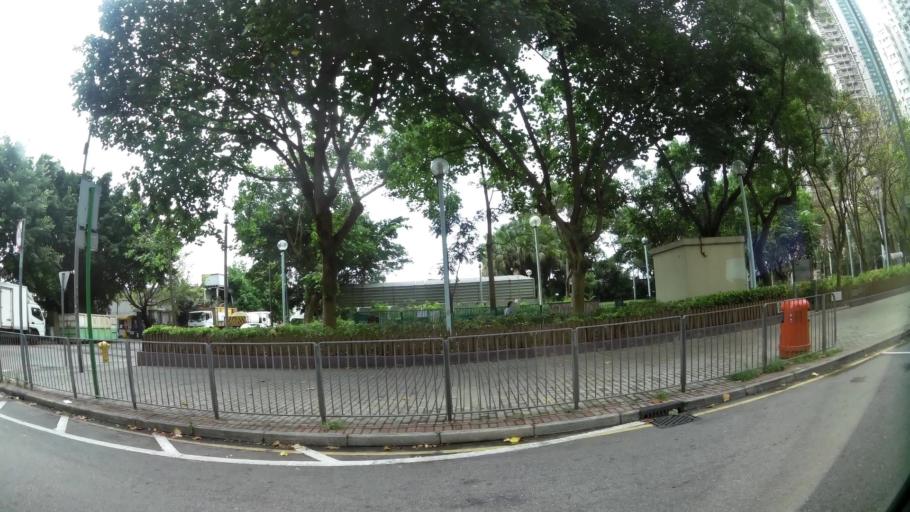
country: HK
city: Hong Kong
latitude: 22.2822
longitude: 114.1249
